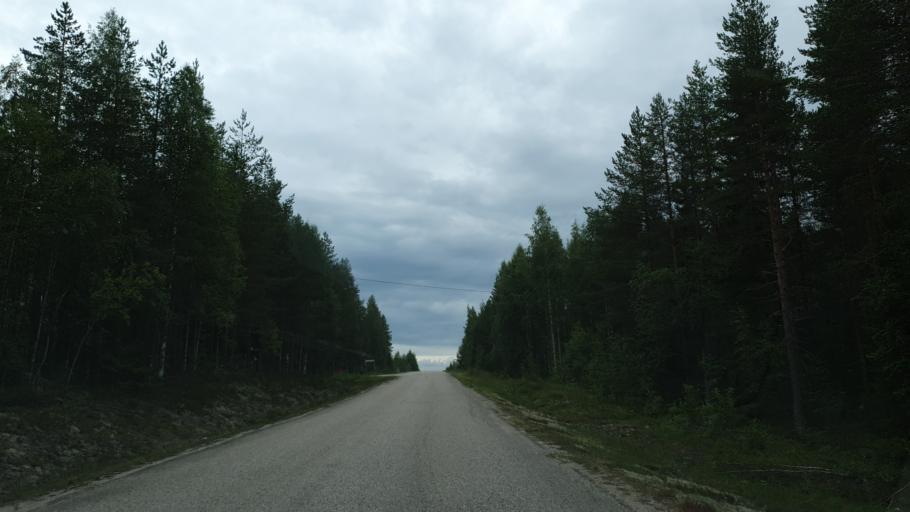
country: FI
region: Kainuu
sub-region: Kehys-Kainuu
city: Kuhmo
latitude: 64.3559
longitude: 29.2036
